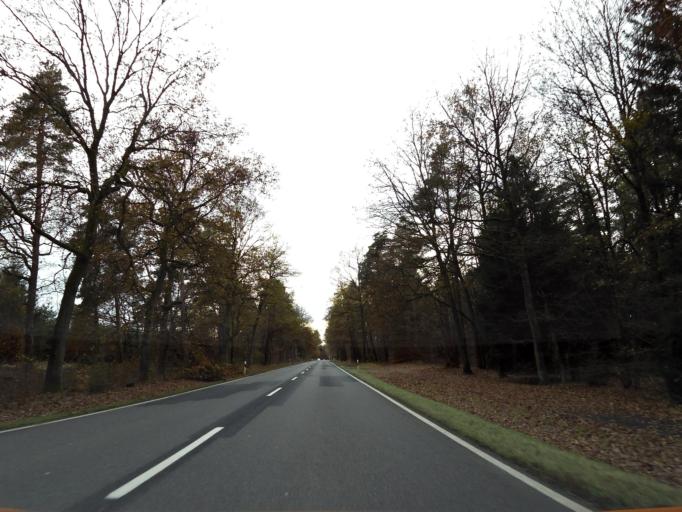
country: DE
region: Lower Saxony
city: Fassberg
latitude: 52.9641
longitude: 10.1930
